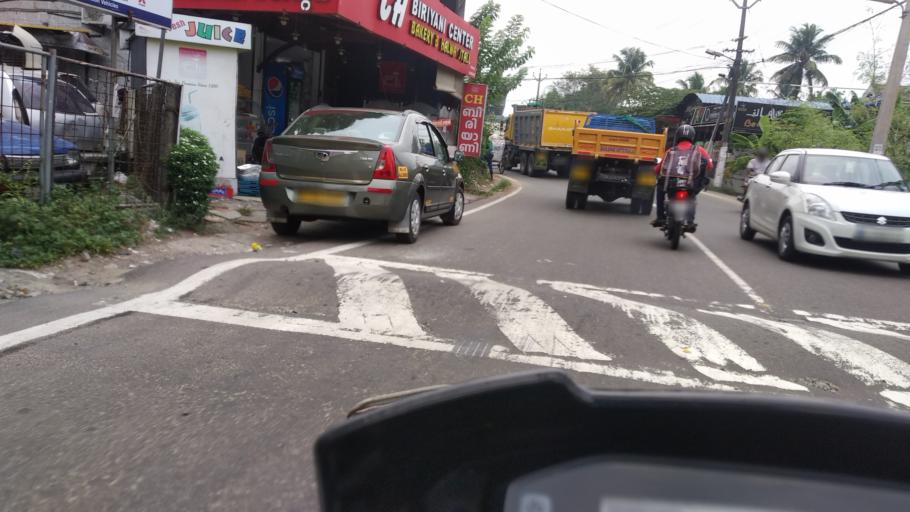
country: IN
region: Kerala
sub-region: Ernakulam
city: Elur
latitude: 10.1502
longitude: 76.2668
